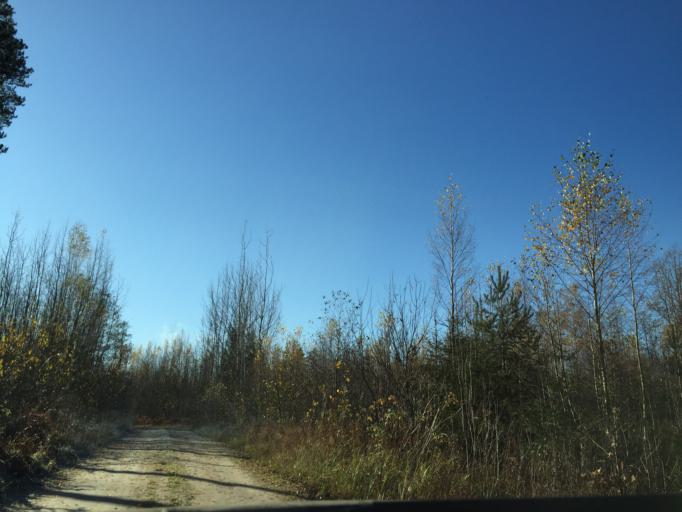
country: LV
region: Aizkraukles Rajons
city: Aizkraukle
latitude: 56.7151
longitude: 25.2995
